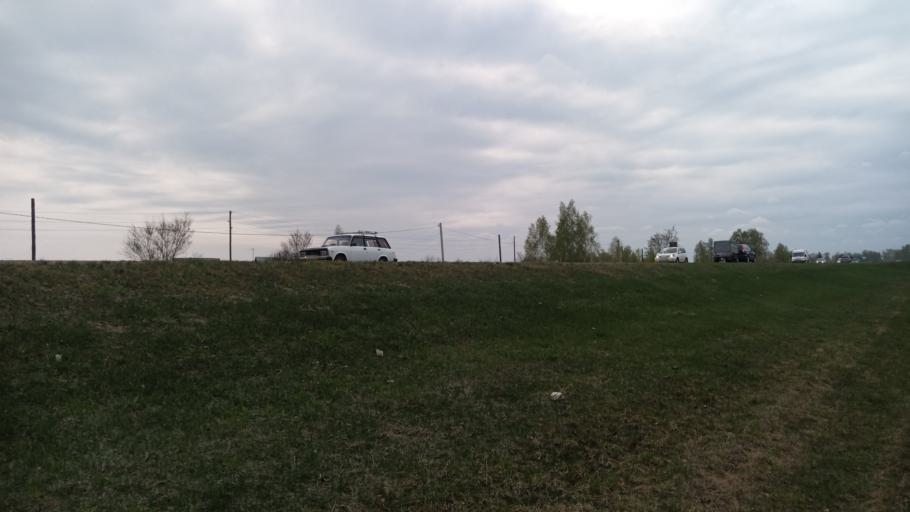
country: RU
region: Altai Krai
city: Yuzhnyy
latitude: 53.2377
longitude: 83.6975
